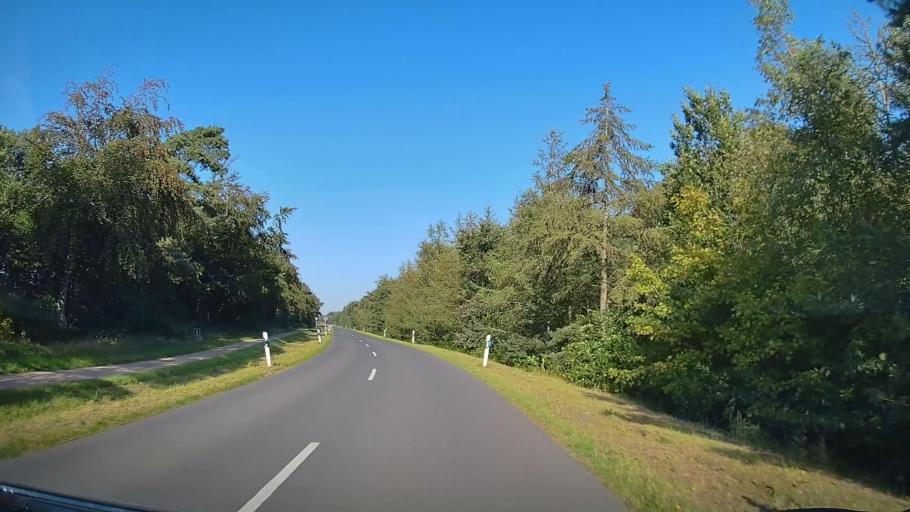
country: DE
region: Lower Saxony
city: Nordholz
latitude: 53.8330
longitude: 8.6122
